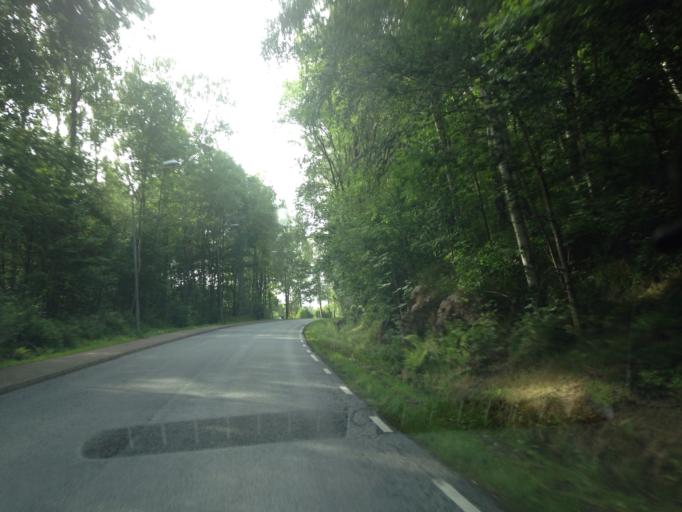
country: SE
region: Vaestra Goetaland
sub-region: Goteborg
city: Goeteborg
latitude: 57.7604
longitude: 11.9820
